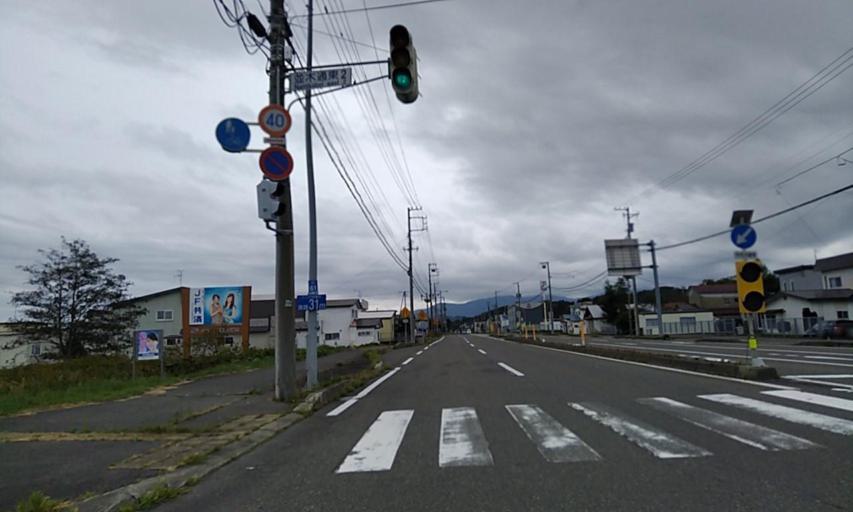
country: JP
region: Hokkaido
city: Obihiro
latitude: 42.3023
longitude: 143.3167
